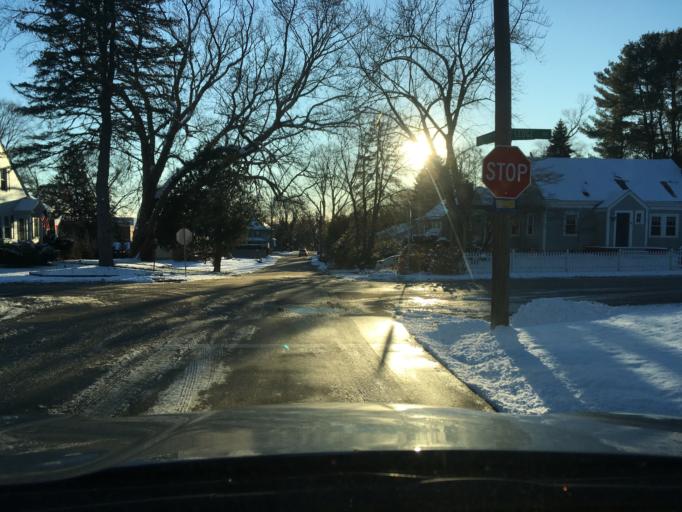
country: US
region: Rhode Island
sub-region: Kent County
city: East Greenwich
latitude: 41.6596
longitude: -71.4578
